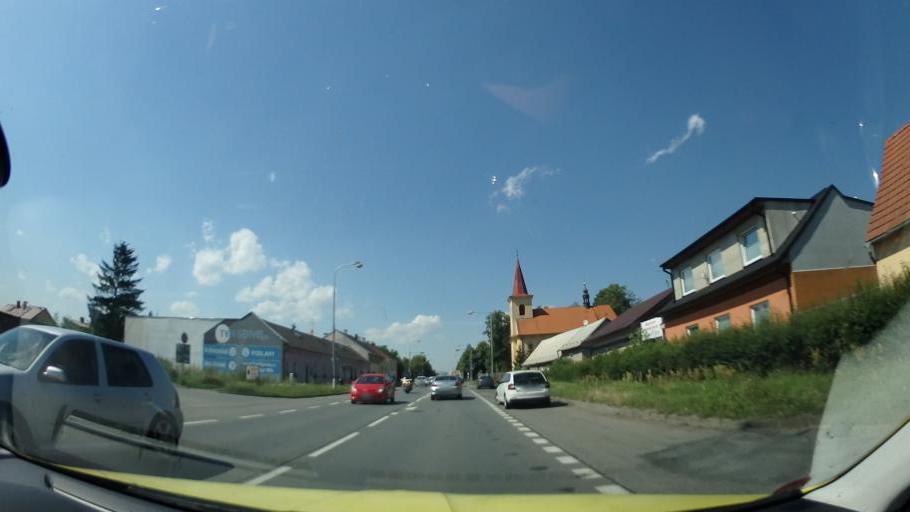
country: CZ
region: Olomoucky
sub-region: Okres Olomouc
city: Olomouc
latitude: 49.5676
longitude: 17.2615
